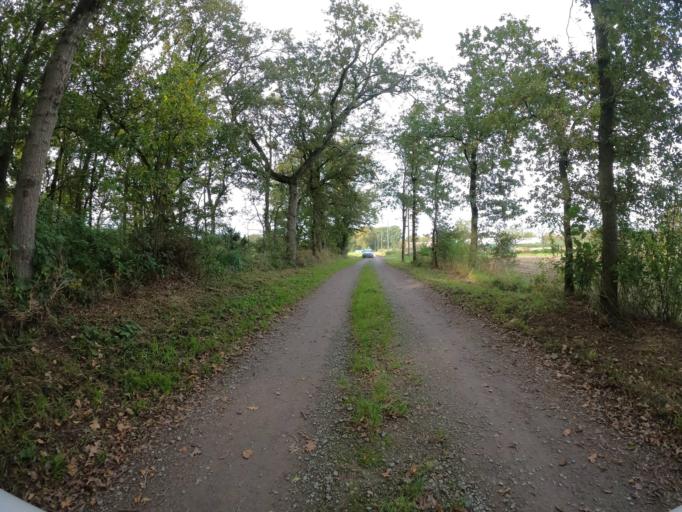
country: DE
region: North Rhine-Westphalia
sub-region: Regierungsbezirk Dusseldorf
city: Schermbeck
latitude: 51.7011
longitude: 6.8565
